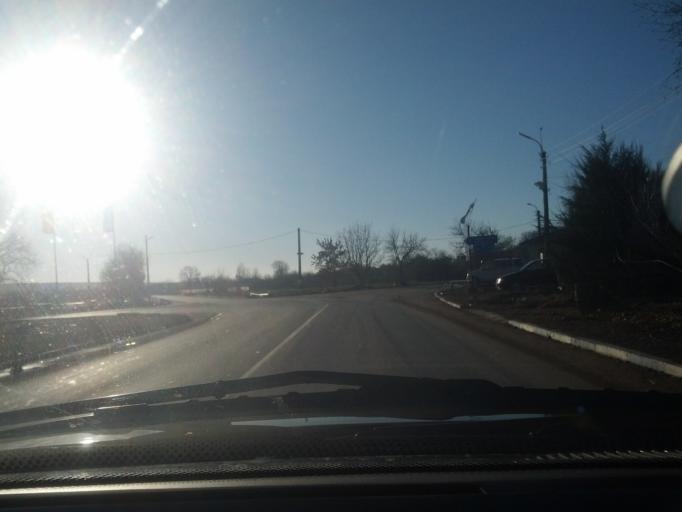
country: BG
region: Vratsa
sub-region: Obshtina Miziya
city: Miziya
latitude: 43.6514
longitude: 23.7608
